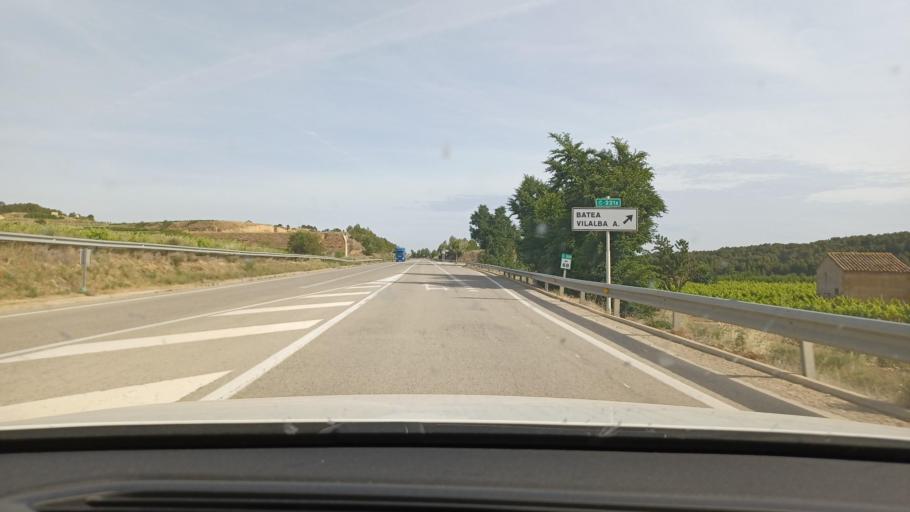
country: ES
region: Catalonia
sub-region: Provincia de Tarragona
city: Batea
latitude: 41.0766
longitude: 0.3292
